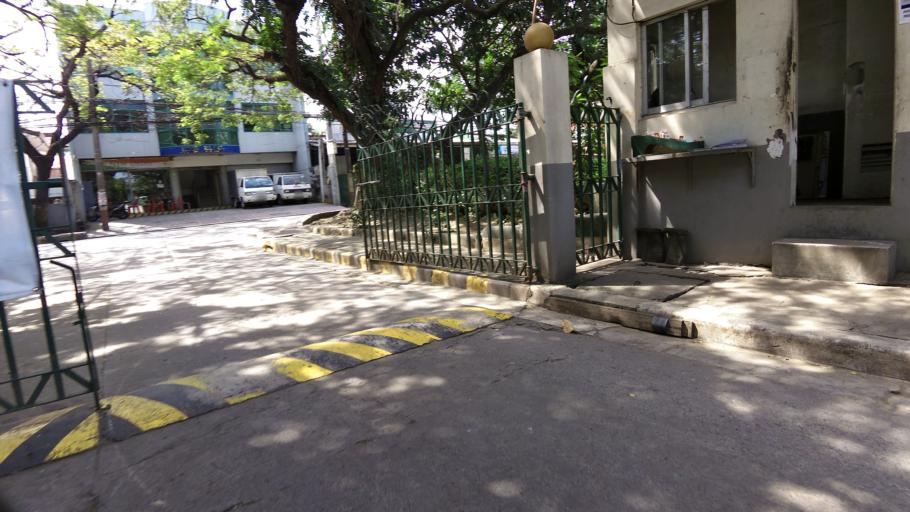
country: PH
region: Calabarzon
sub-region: Province of Rizal
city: Cainta
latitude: 14.5755
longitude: 121.0955
